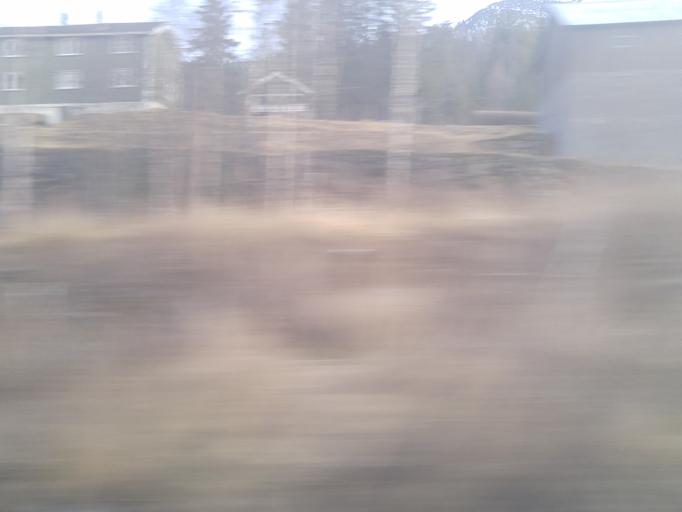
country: NO
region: Oppland
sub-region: Dovre
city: Dovre
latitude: 61.8958
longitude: 9.3938
